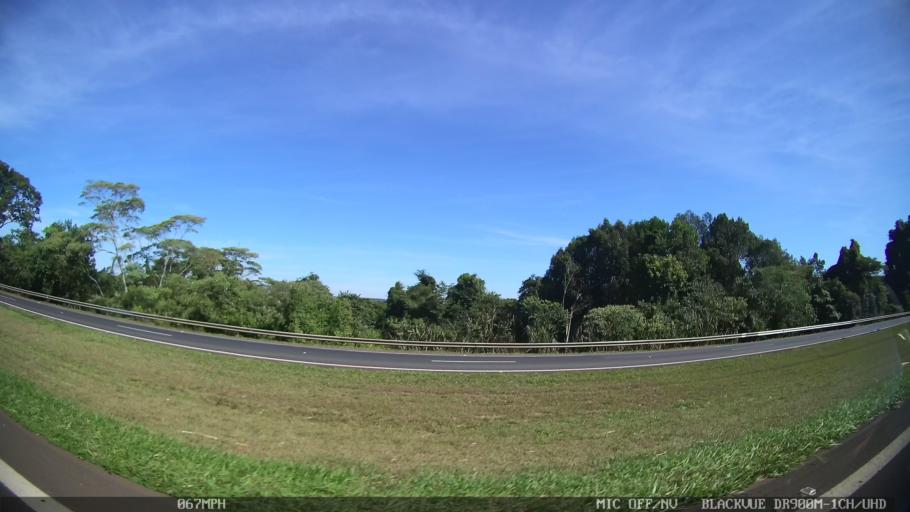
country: BR
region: Sao Paulo
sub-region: Porto Ferreira
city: Porto Ferreira
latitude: -21.8149
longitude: -47.4978
